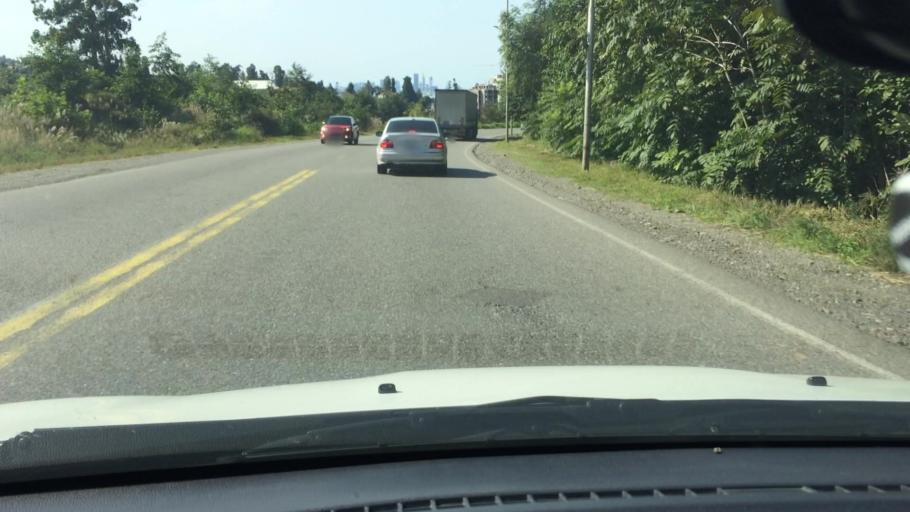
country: GE
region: Ajaria
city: Makhinjauri
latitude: 41.6877
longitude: 41.7104
